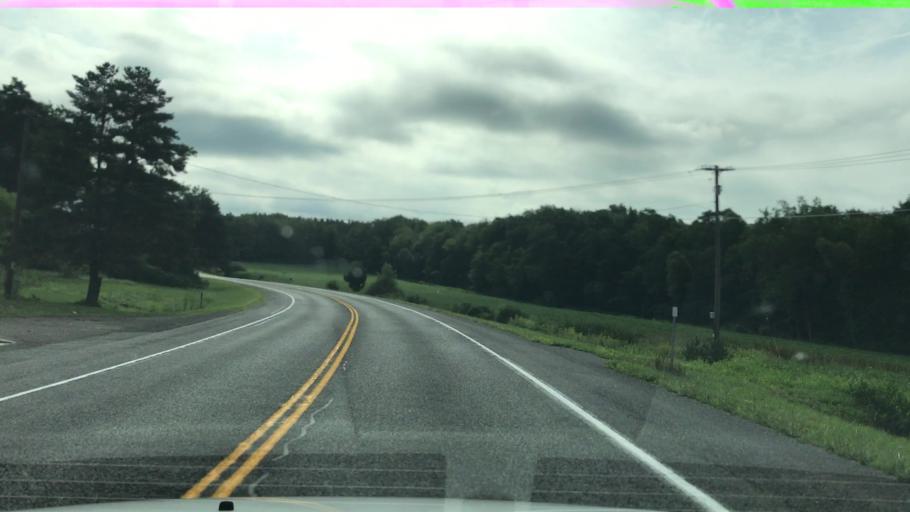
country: US
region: New York
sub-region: Erie County
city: Alden
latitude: 42.8351
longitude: -78.4489
